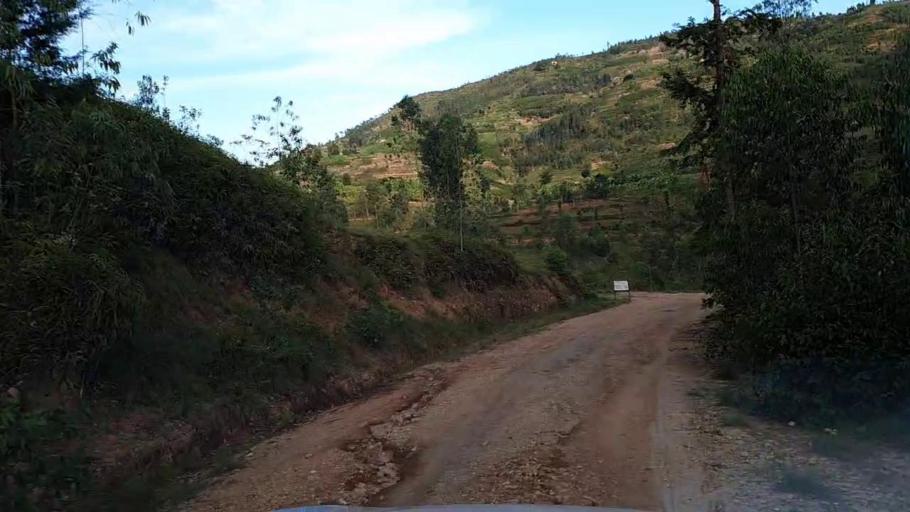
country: RW
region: Southern Province
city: Gikongoro
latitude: -2.4011
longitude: 29.5650
